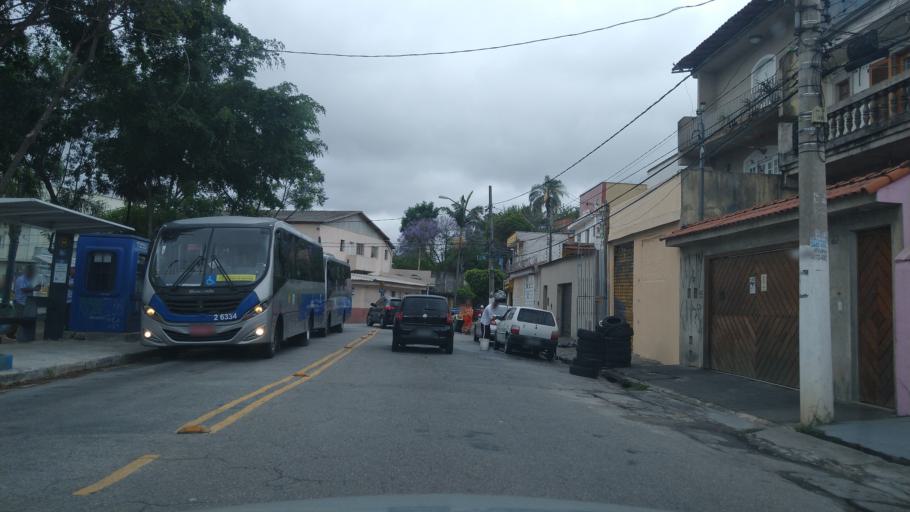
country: BR
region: Sao Paulo
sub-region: Sao Paulo
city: Sao Paulo
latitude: -23.4784
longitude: -46.6232
